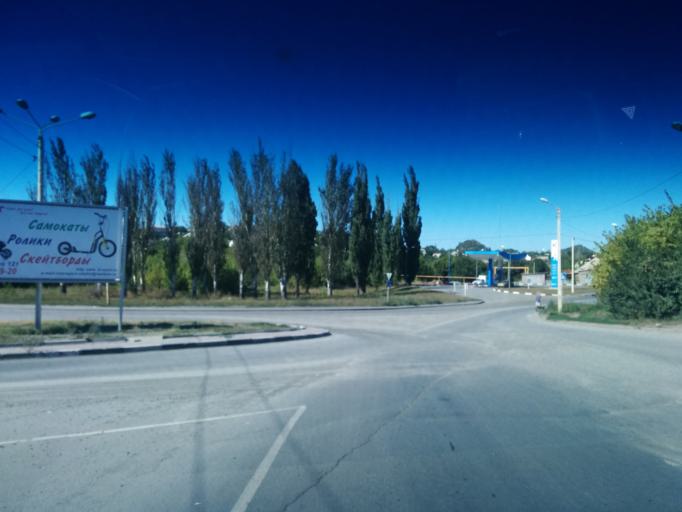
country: RU
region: Rostov
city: Shakhty
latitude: 47.6978
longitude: 40.2386
